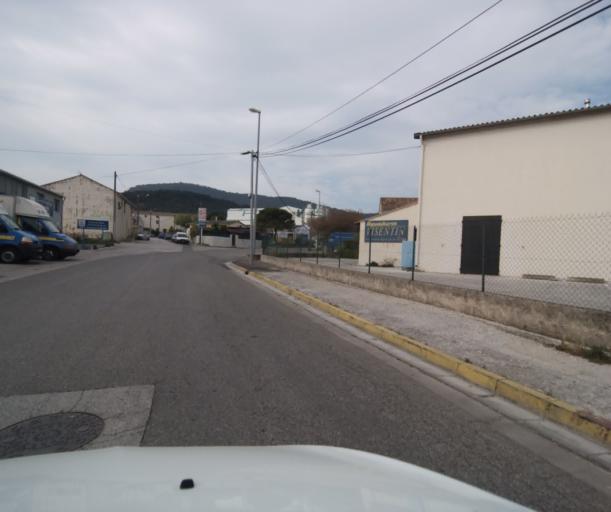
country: FR
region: Provence-Alpes-Cote d'Azur
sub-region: Departement du Var
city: Hyeres
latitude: 43.1125
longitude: 6.1116
